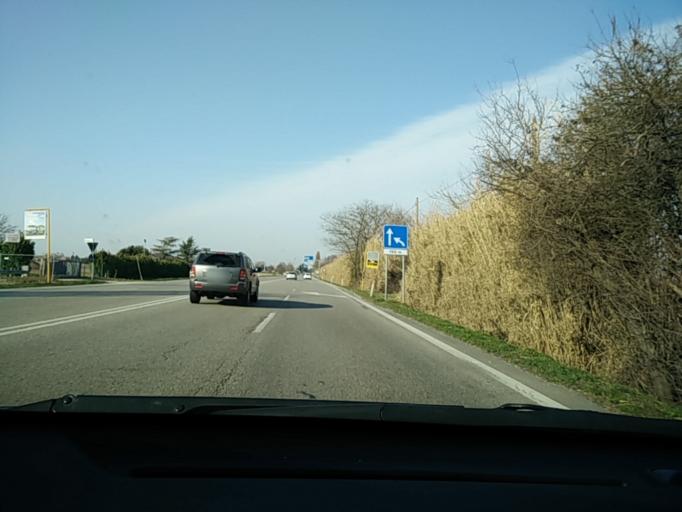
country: IT
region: Veneto
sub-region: Provincia di Venezia
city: San Liberale
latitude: 45.5274
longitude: 12.3812
